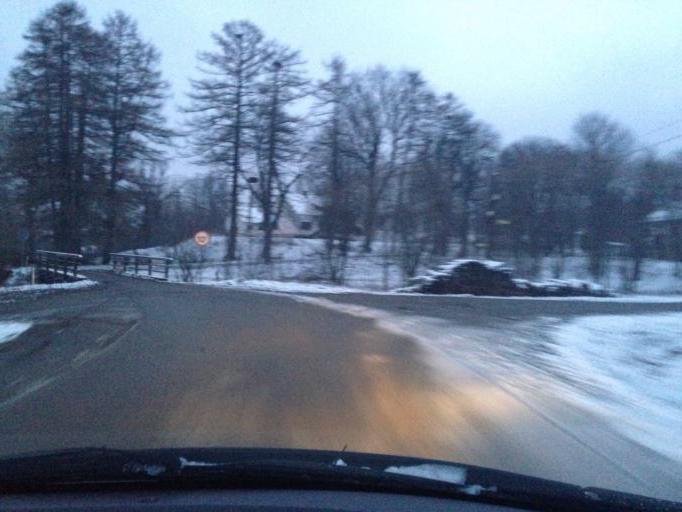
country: PL
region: Subcarpathian Voivodeship
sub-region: Powiat jasielski
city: Krempna
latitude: 49.5286
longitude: 21.5550
